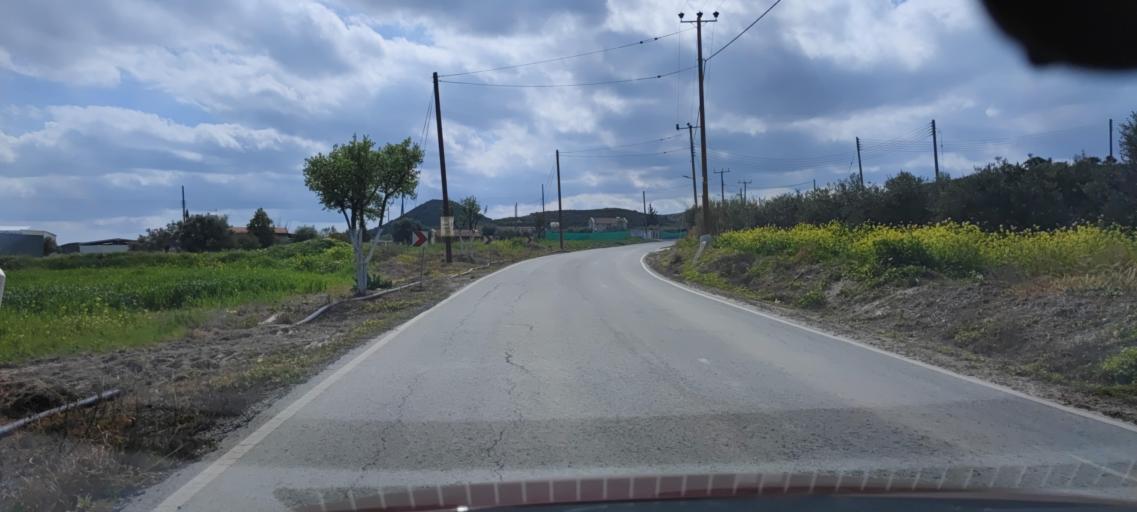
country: CY
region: Lefkosia
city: Pera
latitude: 35.0211
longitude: 33.3022
